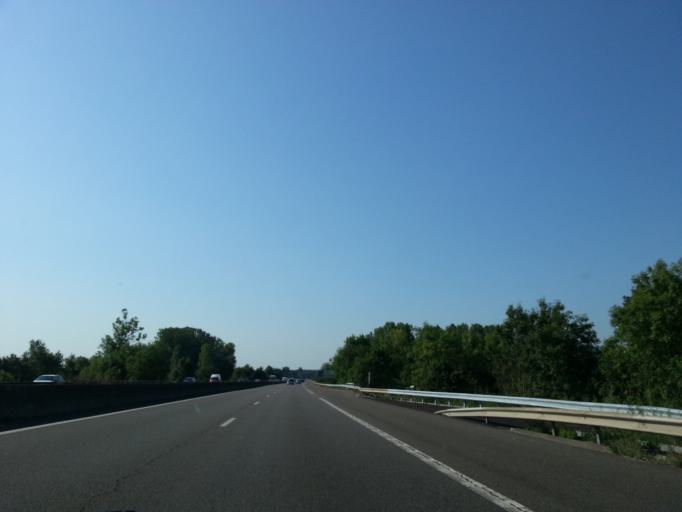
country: FR
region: Alsace
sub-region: Departement du Bas-Rhin
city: Brumath
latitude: 48.7393
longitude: 7.6880
